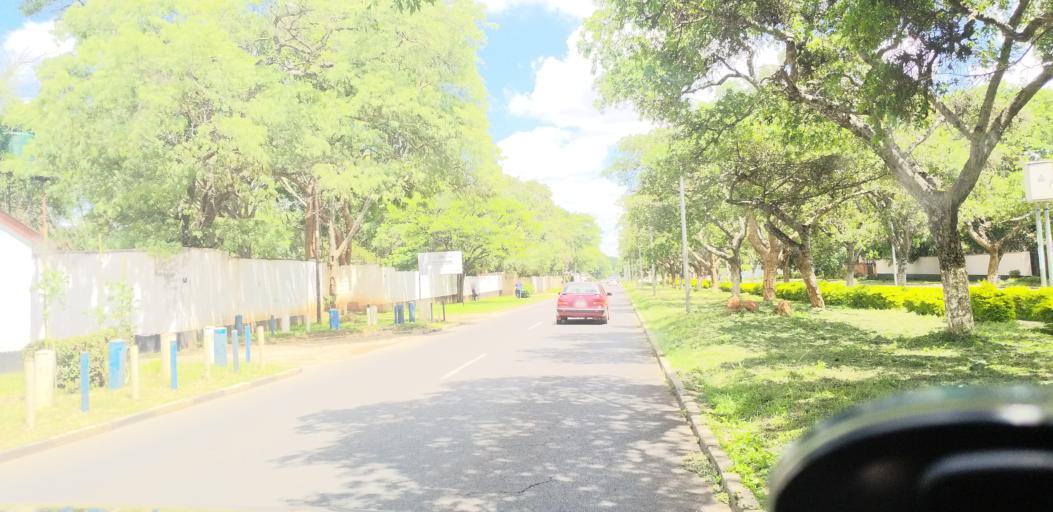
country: ZM
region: Lusaka
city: Lusaka
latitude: -15.4286
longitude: 28.3211
